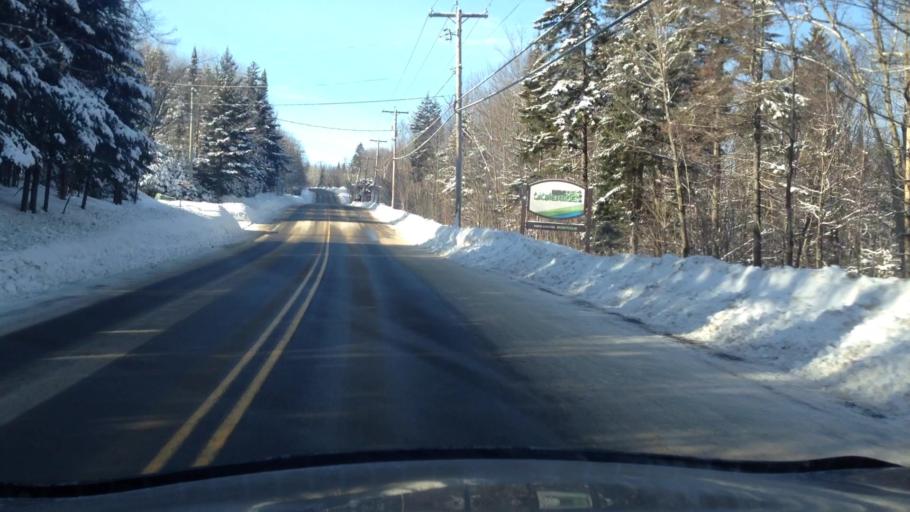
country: CA
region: Quebec
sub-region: Laurentides
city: Sainte-Agathe-des-Monts
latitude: 45.9348
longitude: -74.4365
